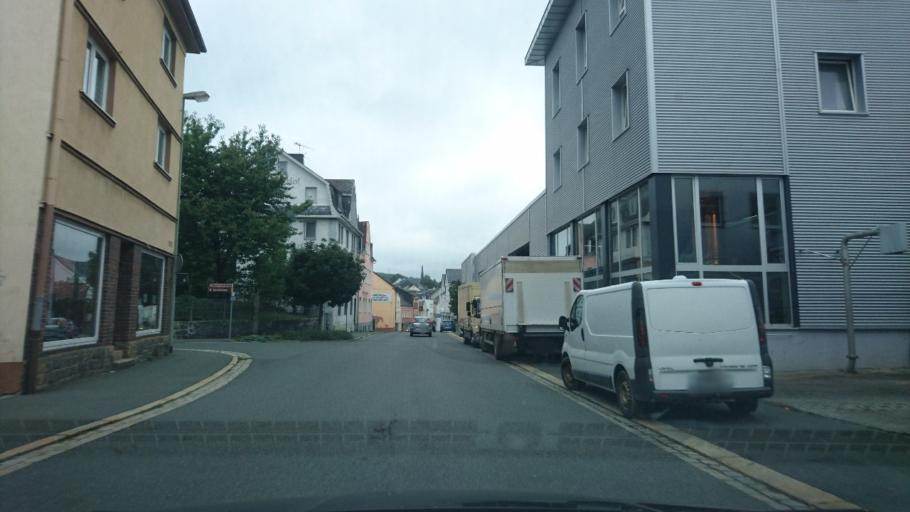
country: DE
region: Bavaria
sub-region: Upper Franconia
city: Naila
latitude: 50.3274
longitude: 11.7116
